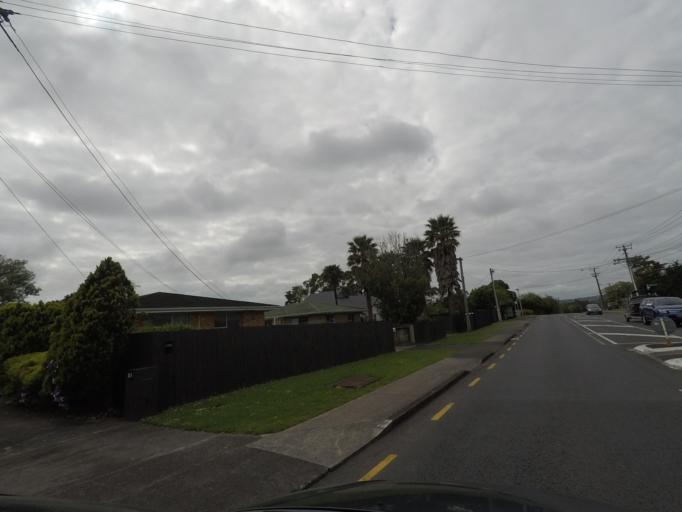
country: NZ
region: Auckland
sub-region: Auckland
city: Rosebank
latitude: -36.8475
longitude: 174.6082
